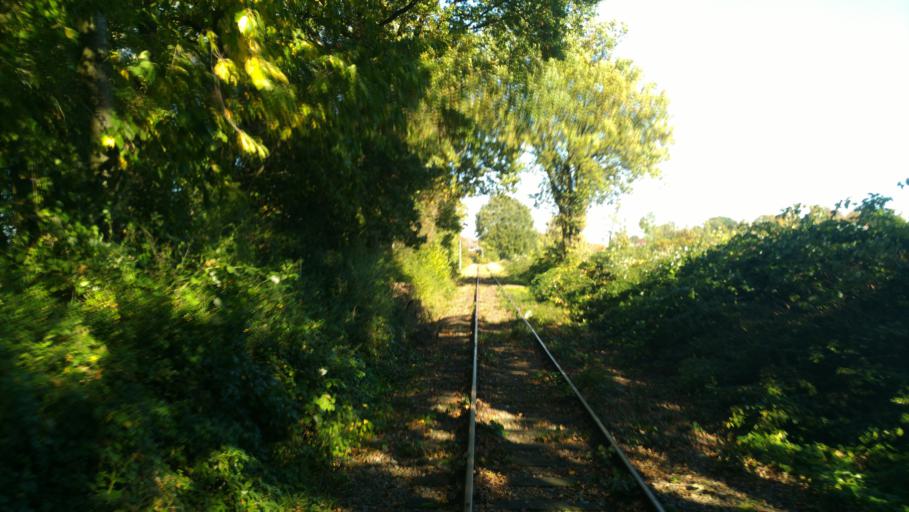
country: DE
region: Lower Saxony
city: Obernkirchen
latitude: 52.2885
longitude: 9.1444
